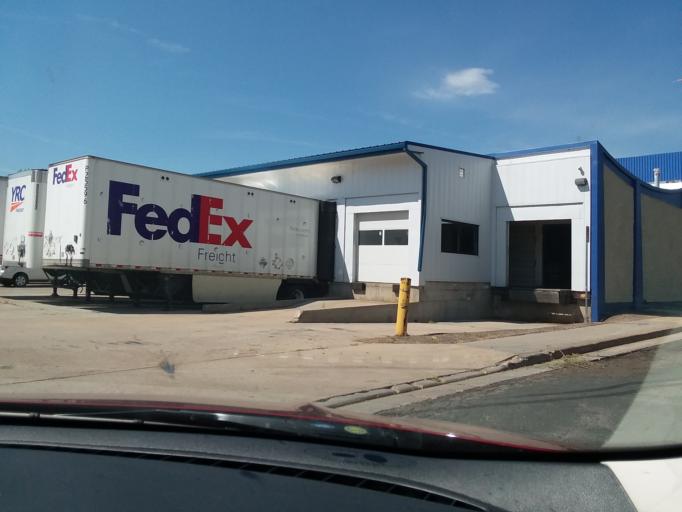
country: US
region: Colorado
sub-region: Larimer County
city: Loveland
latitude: 40.4082
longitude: -105.1026
